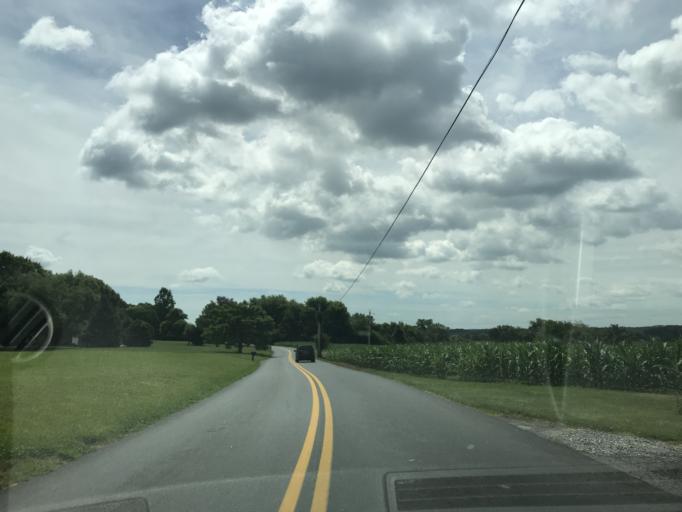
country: US
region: Maryland
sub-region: Carroll County
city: Hampstead
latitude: 39.6361
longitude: -76.8068
